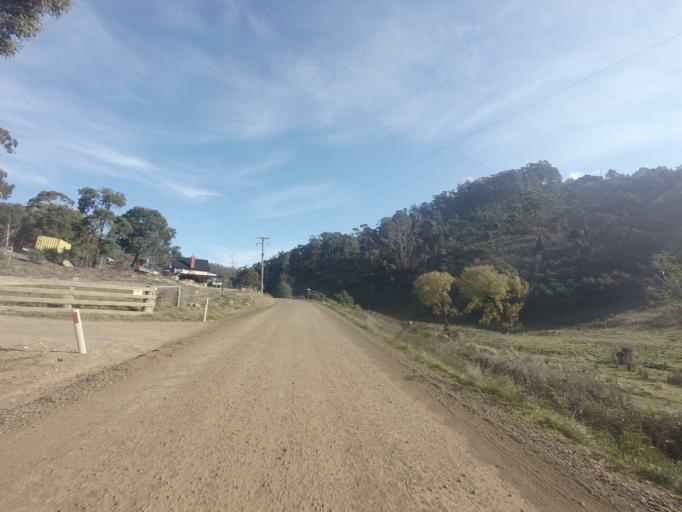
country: AU
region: Tasmania
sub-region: Sorell
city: Sorell
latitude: -42.5057
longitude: 147.4294
